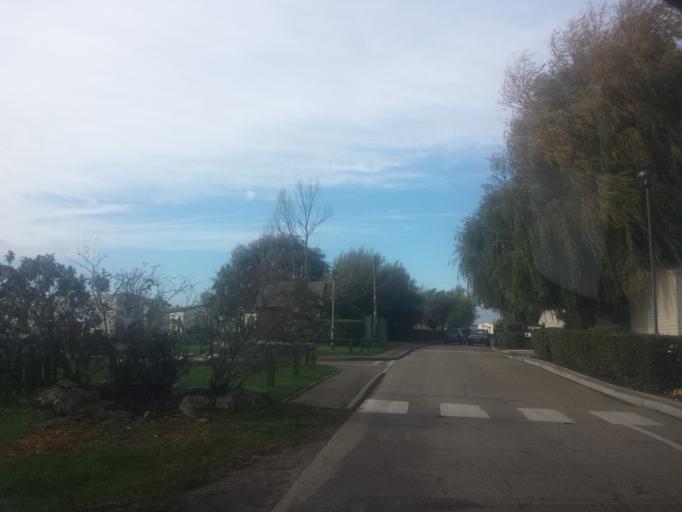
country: GB
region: England
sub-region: Essex
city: Brightlingsea
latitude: 51.7993
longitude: 1.0260
